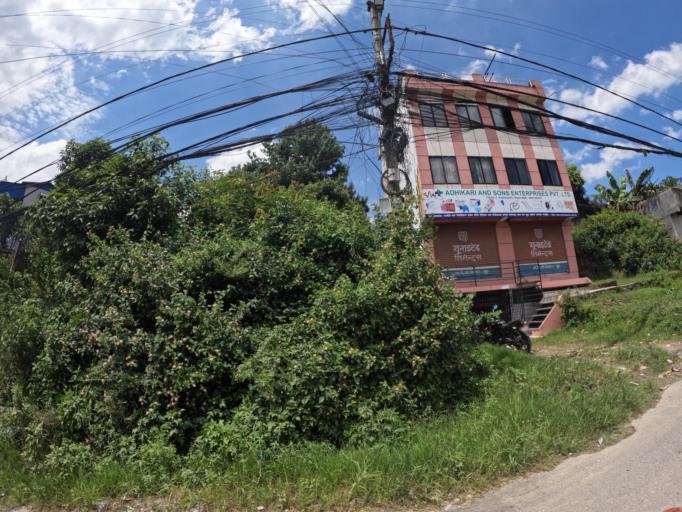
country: NP
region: Central Region
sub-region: Bagmati Zone
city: Kathmandu
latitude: 27.7580
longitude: 85.3276
